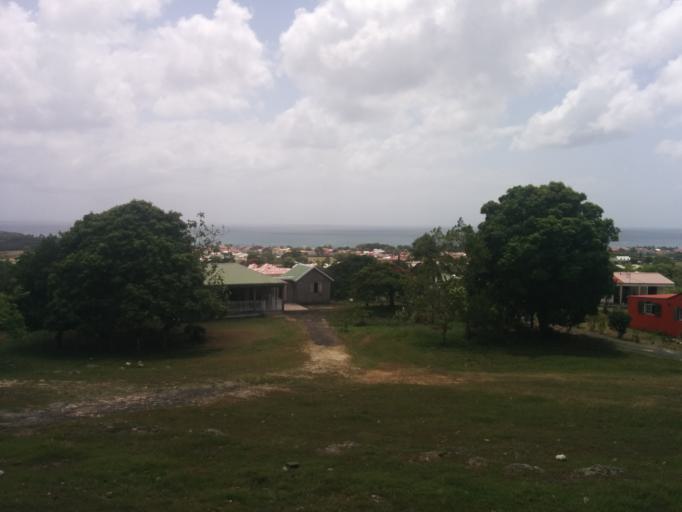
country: GP
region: Guadeloupe
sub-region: Guadeloupe
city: Grand-Bourg
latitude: 15.9536
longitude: -61.3073
